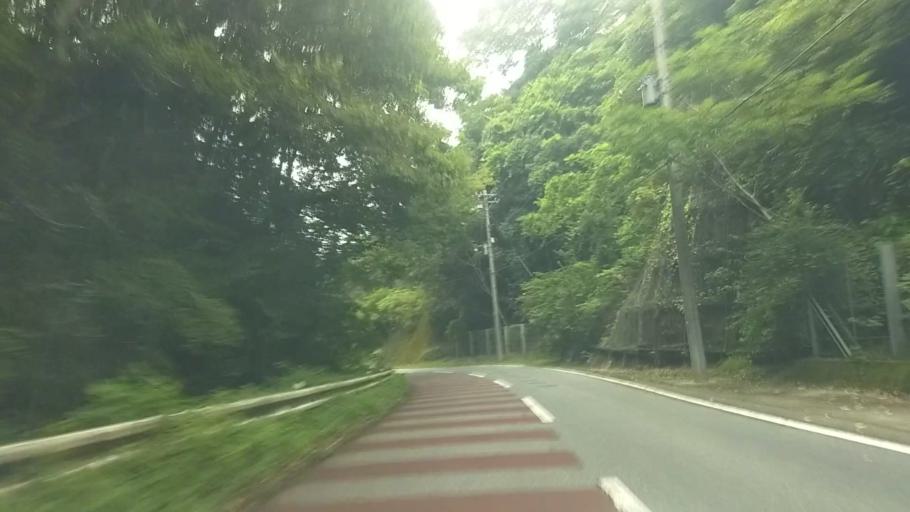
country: JP
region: Chiba
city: Kawaguchi
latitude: 35.2354
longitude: 140.0314
